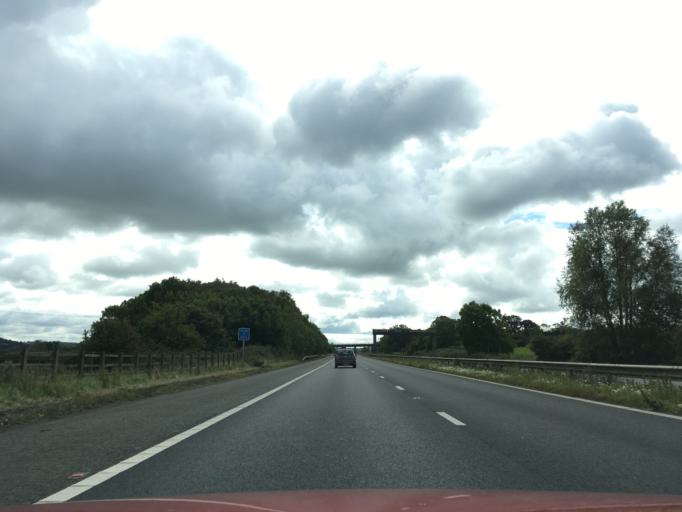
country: GB
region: England
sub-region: South Gloucestershire
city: Almondsbury
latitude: 51.5923
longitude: -2.6036
